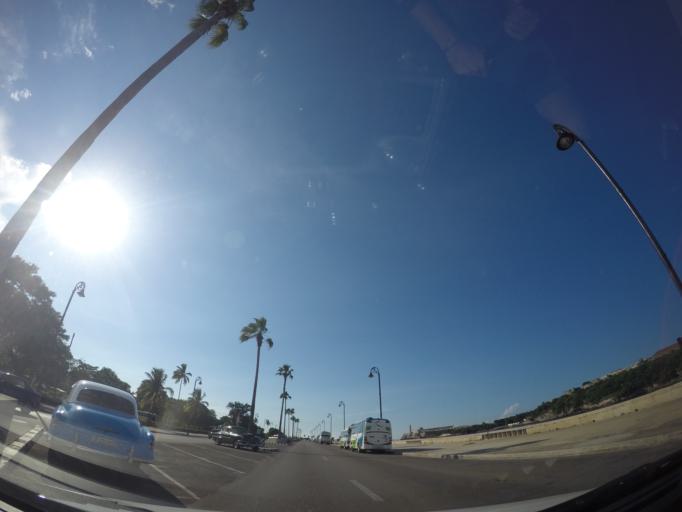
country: CU
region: La Habana
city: La Habana Vieja
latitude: 23.1428
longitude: -82.3508
